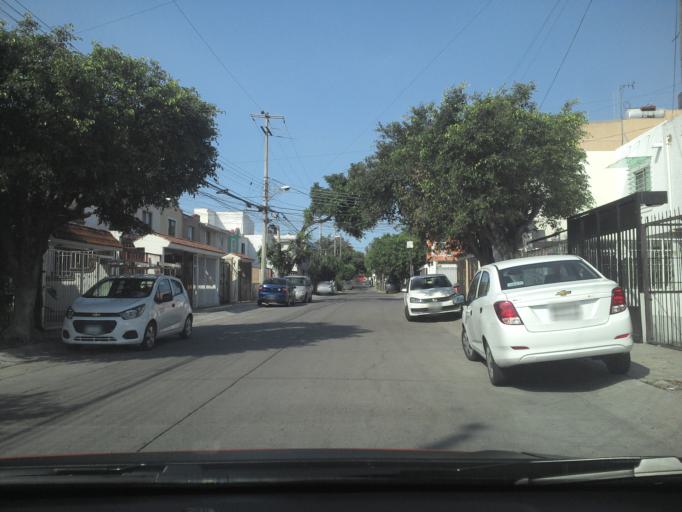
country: MX
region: Jalisco
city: Guadalajara
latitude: 20.6490
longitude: -103.4415
